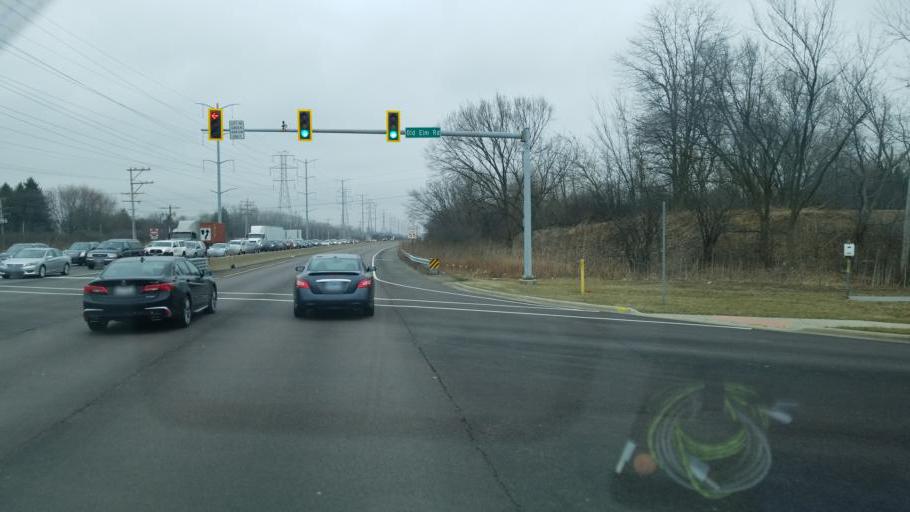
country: US
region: Illinois
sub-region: Lake County
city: Bannockburn
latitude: 42.2180
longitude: -87.8454
